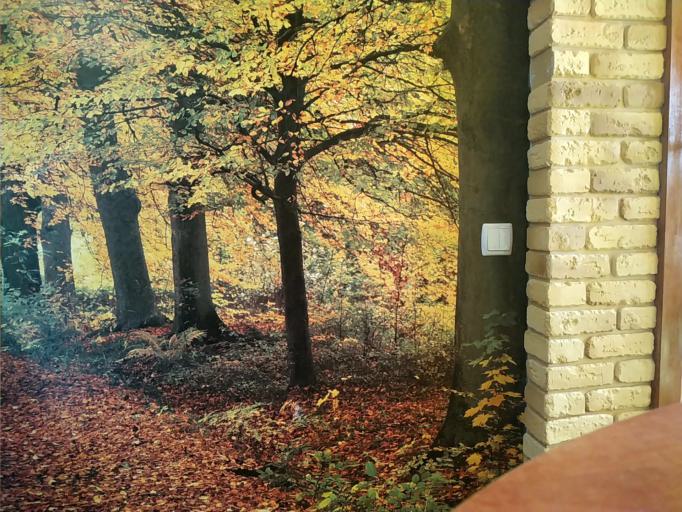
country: RU
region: Jaroslavl
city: Kukoboy
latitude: 58.8841
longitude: 39.7082
